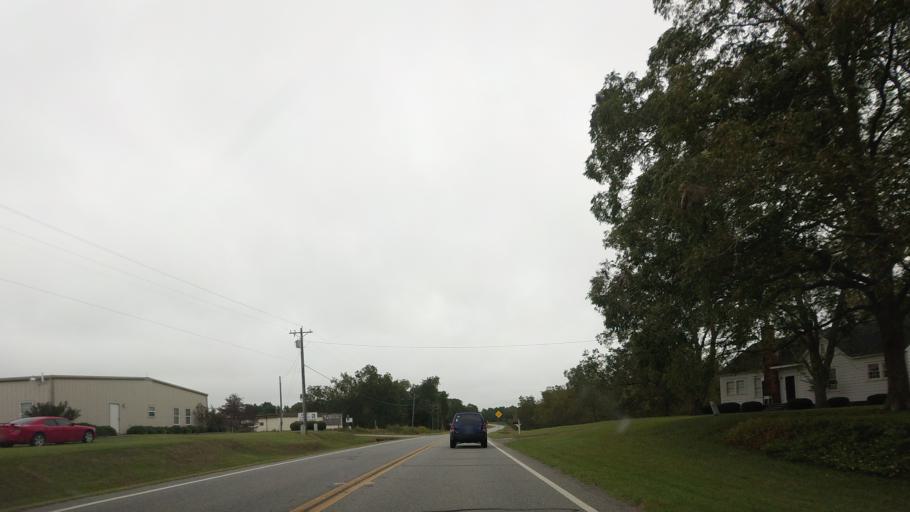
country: US
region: Georgia
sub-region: Irwin County
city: Ocilla
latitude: 31.5778
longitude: -83.2526
